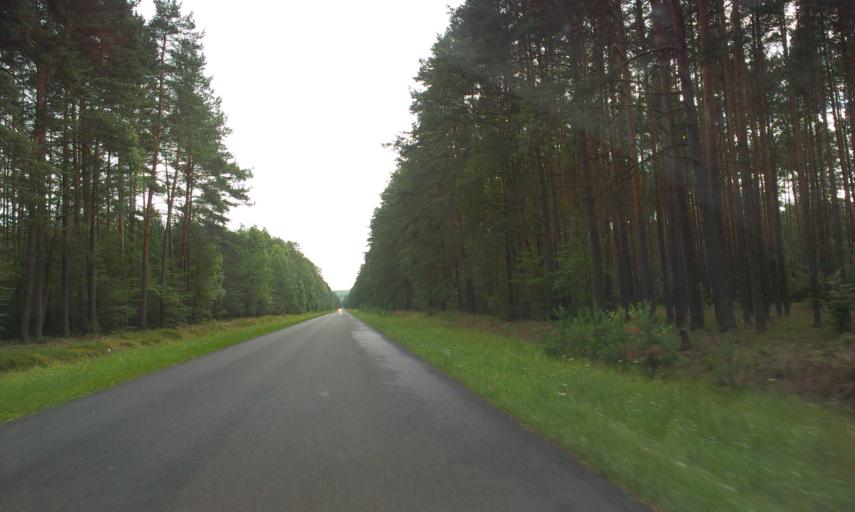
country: PL
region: Greater Poland Voivodeship
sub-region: Powiat zlotowski
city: Okonek
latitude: 53.5109
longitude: 16.9762
